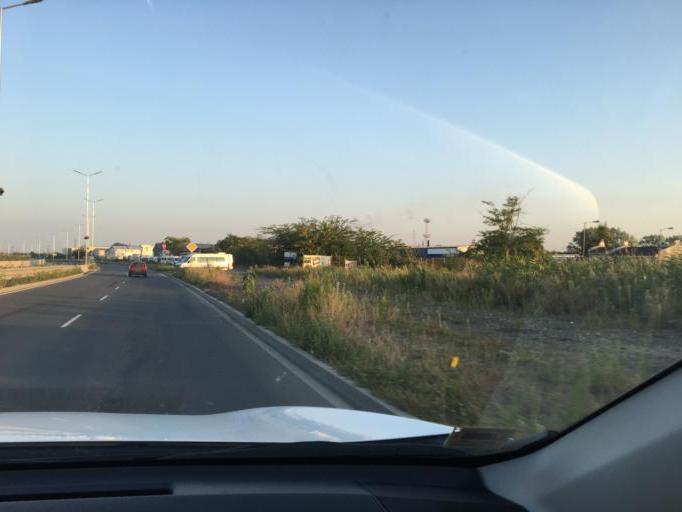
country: BG
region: Burgas
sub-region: Obshtina Burgas
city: Burgas
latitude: 42.5092
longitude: 27.4421
